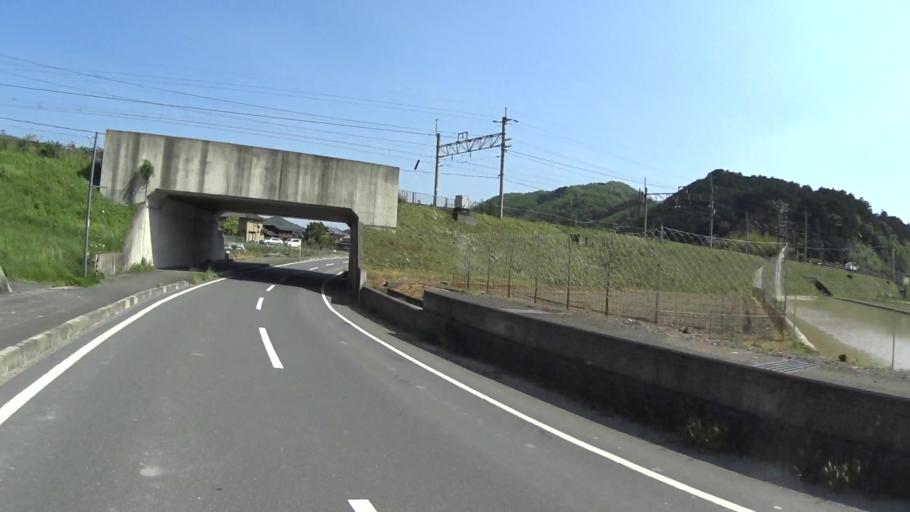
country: JP
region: Kyoto
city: Kameoka
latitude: 35.1343
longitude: 135.4923
